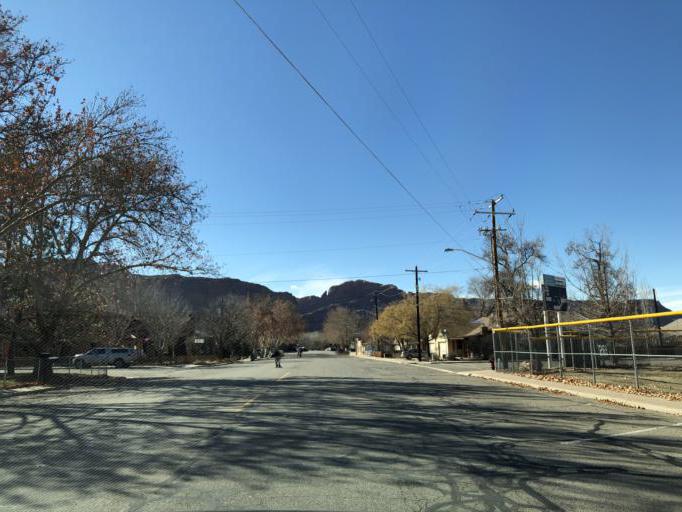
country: US
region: Utah
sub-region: Grand County
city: Moab
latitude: 38.5718
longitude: -109.5462
